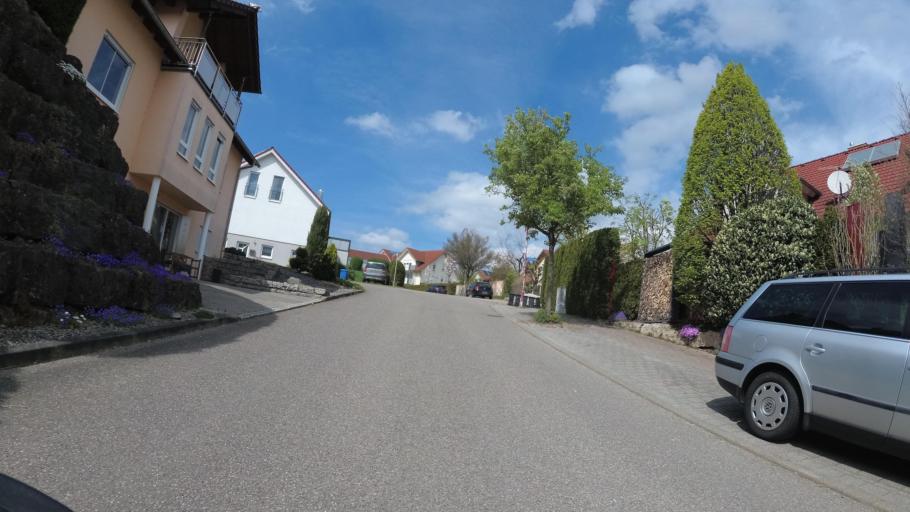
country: DE
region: Baden-Wuerttemberg
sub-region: Regierungsbezirk Stuttgart
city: Neuenstadt am Kocher
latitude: 49.2454
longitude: 9.4011
